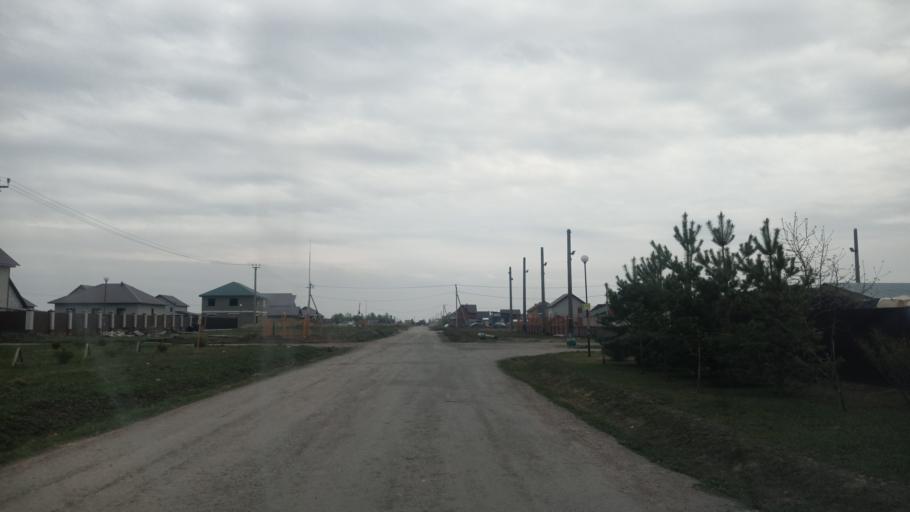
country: RU
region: Altai Krai
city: Yuzhnyy
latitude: 53.2226
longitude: 83.6928
